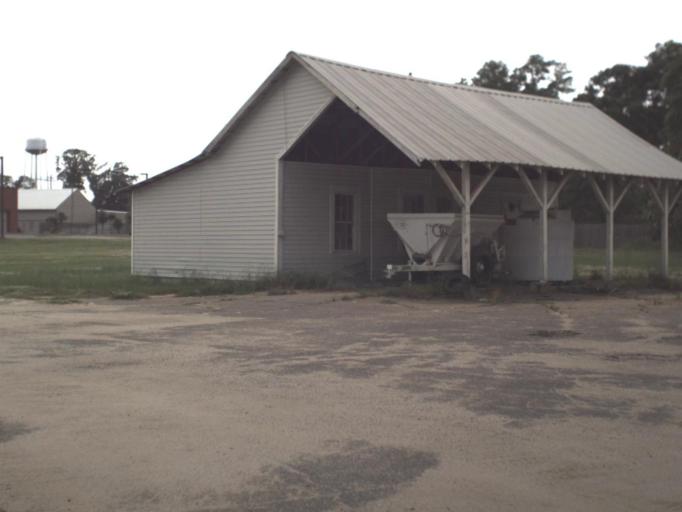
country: US
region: Florida
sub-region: Escambia County
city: Century
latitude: 30.9539
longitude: -87.1497
